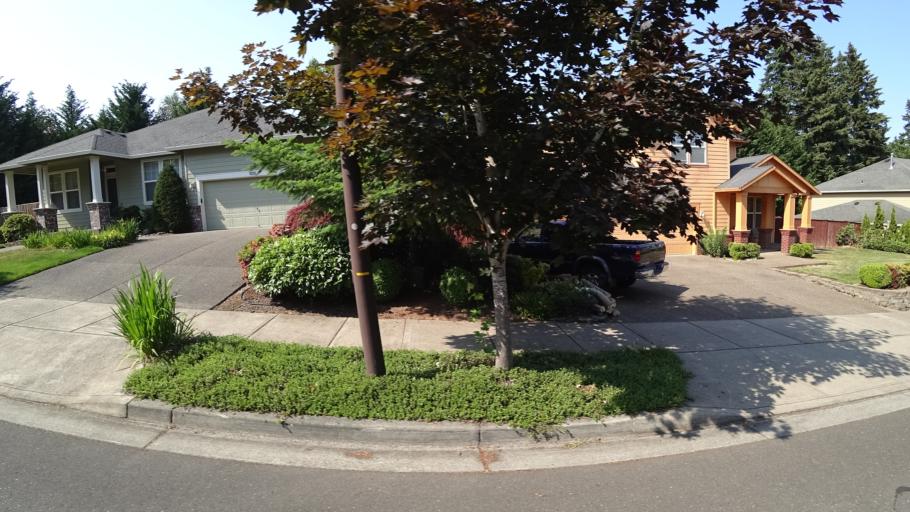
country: US
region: Oregon
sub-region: Clackamas County
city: Happy Valley
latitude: 45.4401
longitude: -122.5371
